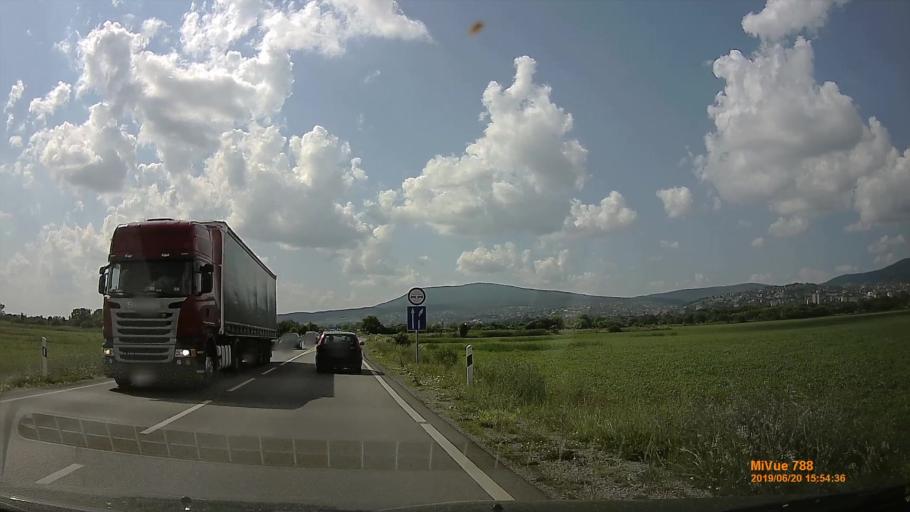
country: HU
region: Baranya
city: Pecs
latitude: 46.0495
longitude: 18.2037
